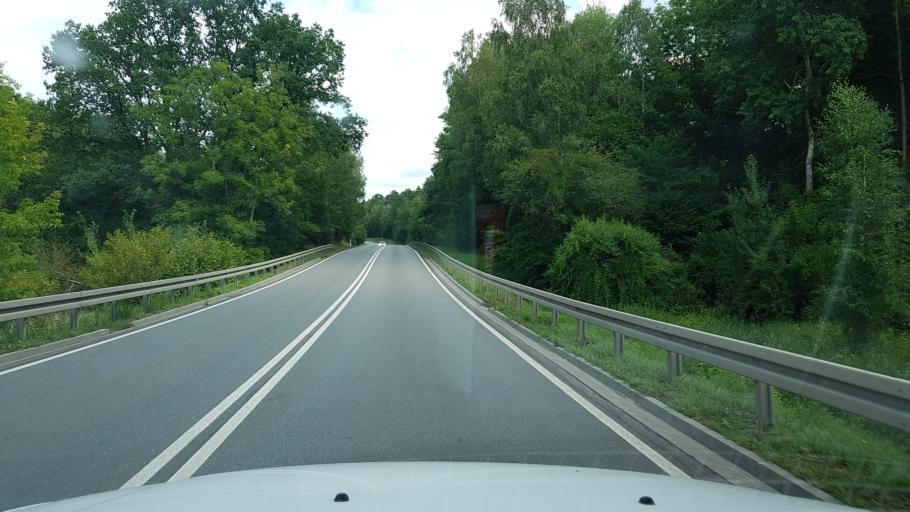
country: PL
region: West Pomeranian Voivodeship
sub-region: Powiat walecki
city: Walcz
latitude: 53.2890
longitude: 16.5158
